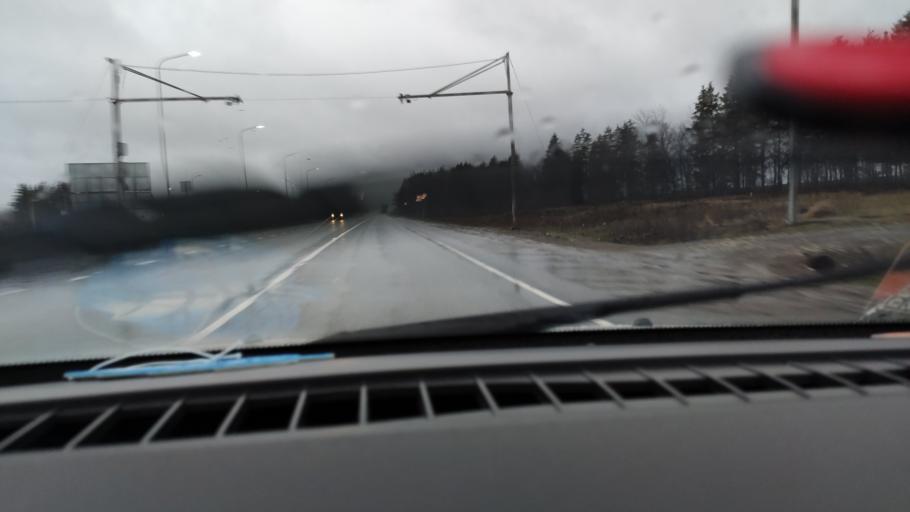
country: RU
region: Tatarstan
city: Mendeleyevsk
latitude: 56.0266
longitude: 52.3686
